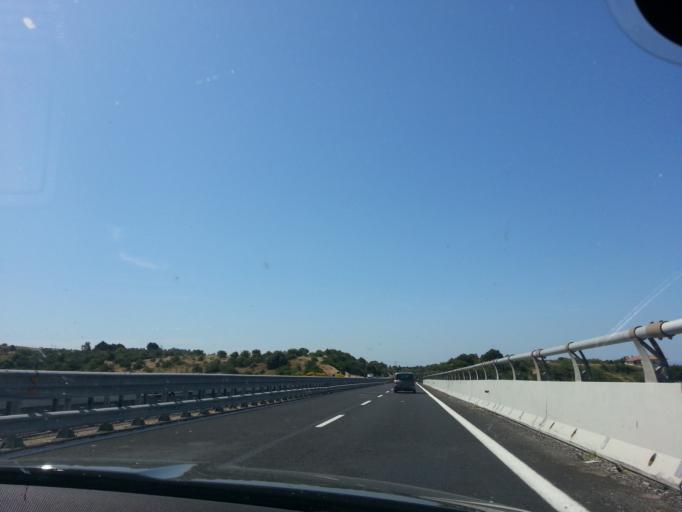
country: IT
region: Latium
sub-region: Citta metropolitana di Roma Capitale
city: Civitavecchia
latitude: 42.0929
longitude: 11.8283
